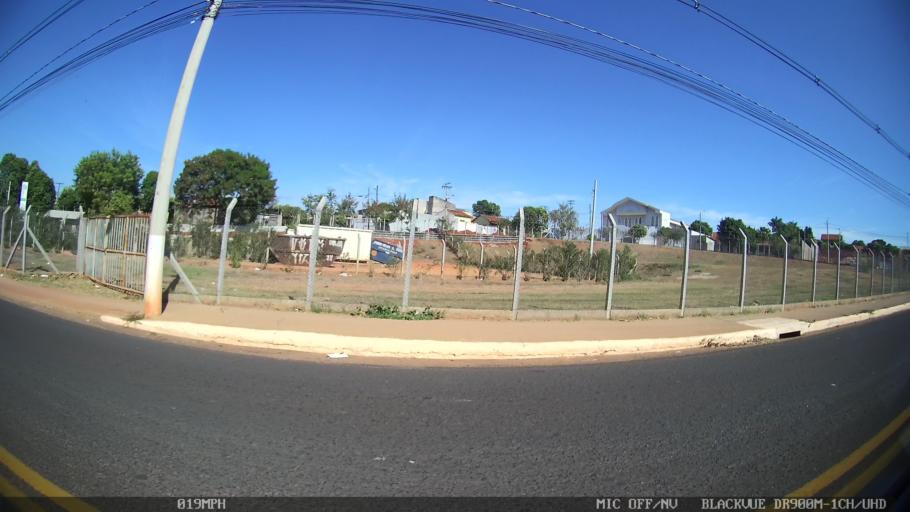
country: BR
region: Sao Paulo
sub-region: Sao Jose Do Rio Preto
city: Sao Jose do Rio Preto
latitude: -20.7694
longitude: -49.4185
